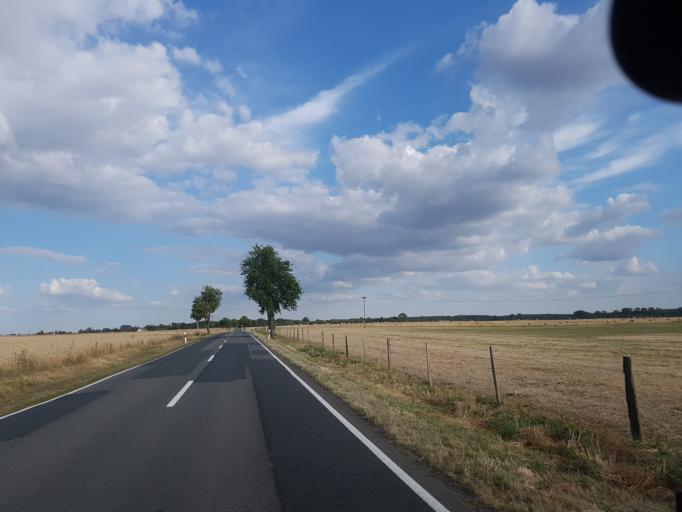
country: DE
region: Brandenburg
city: Schlieben
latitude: 51.7336
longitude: 13.3051
